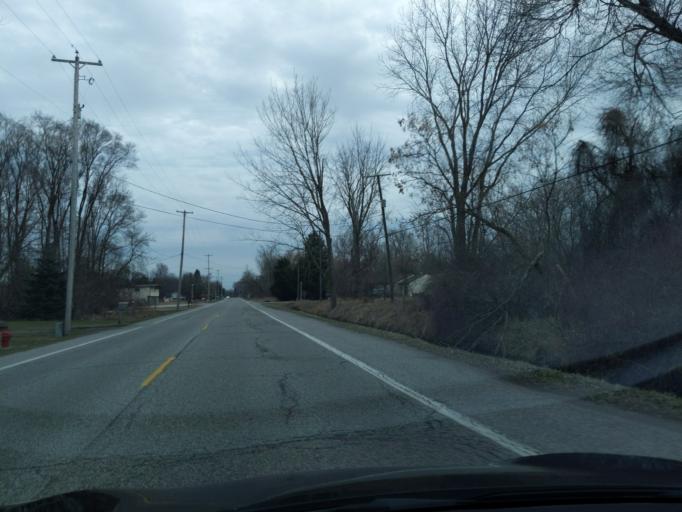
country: US
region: Michigan
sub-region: Bay County
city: Bay City
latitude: 43.6638
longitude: -83.9124
